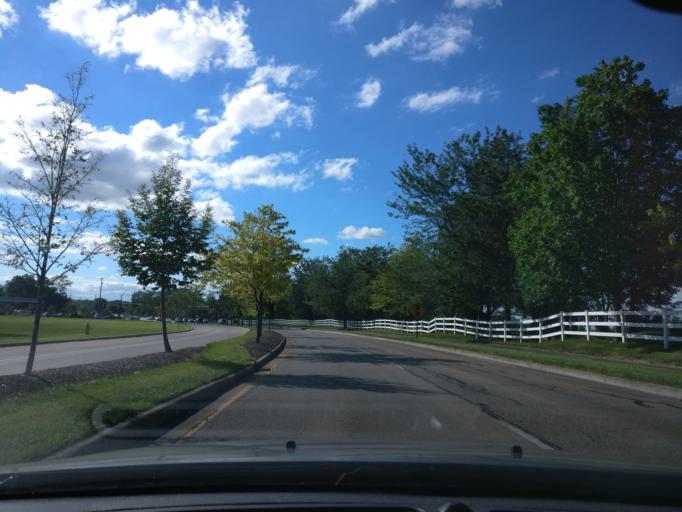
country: US
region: Ohio
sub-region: Warren County
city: Five Points
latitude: 39.5942
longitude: -84.1981
